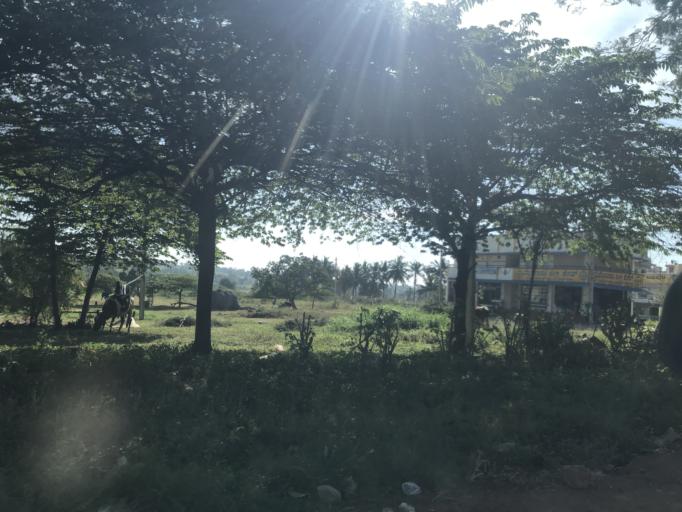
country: IN
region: Karnataka
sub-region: Mysore
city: Mysore
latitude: 12.2059
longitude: 76.5557
